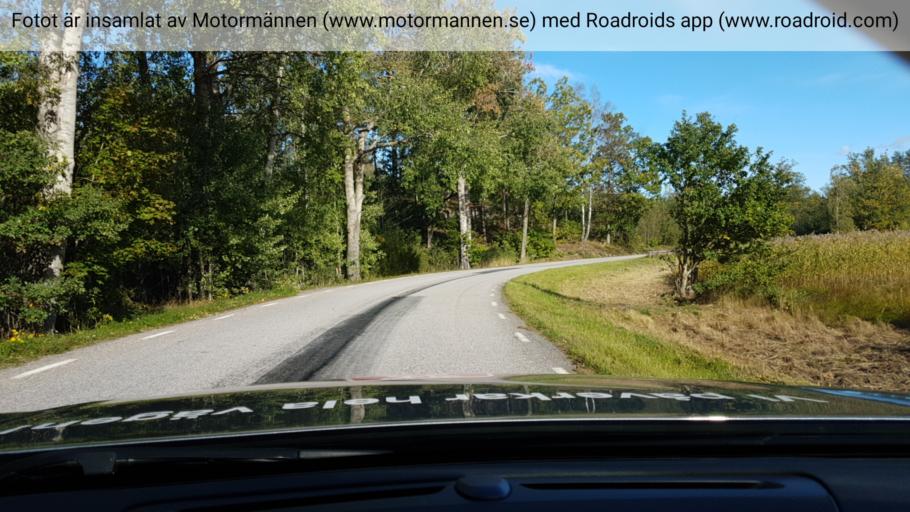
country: SE
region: OEstergoetland
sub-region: Valdemarsviks Kommun
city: Valdemarsvik
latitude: 58.1091
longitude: 16.6445
